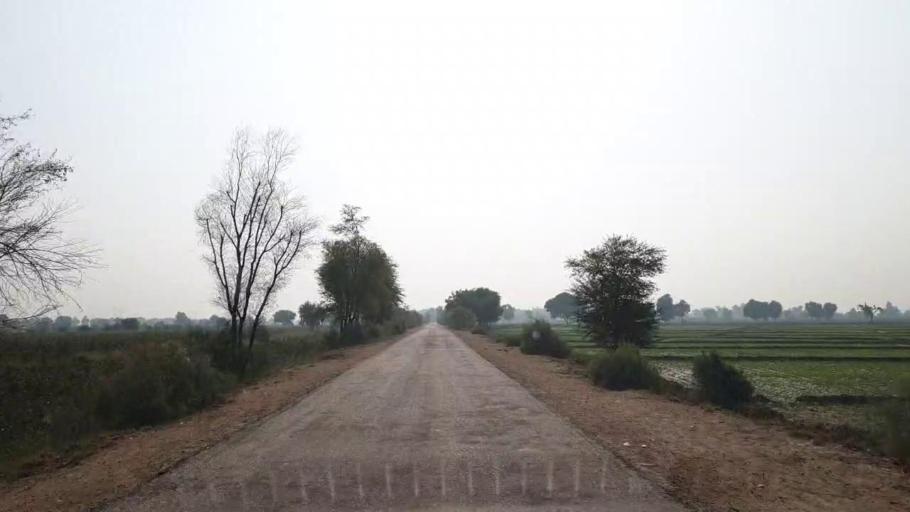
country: PK
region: Sindh
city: Sehwan
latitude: 26.4716
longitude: 67.7751
